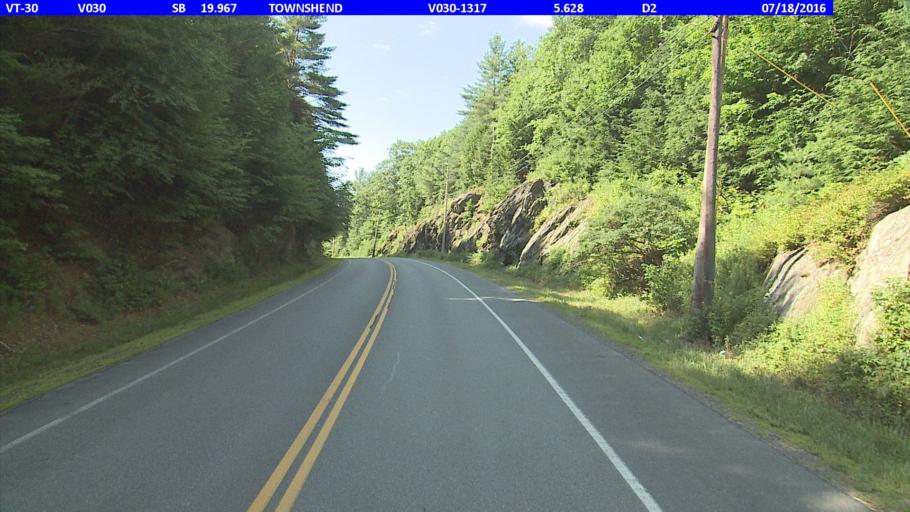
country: US
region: Vermont
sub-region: Windham County
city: Newfane
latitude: 43.0734
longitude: -72.7054
